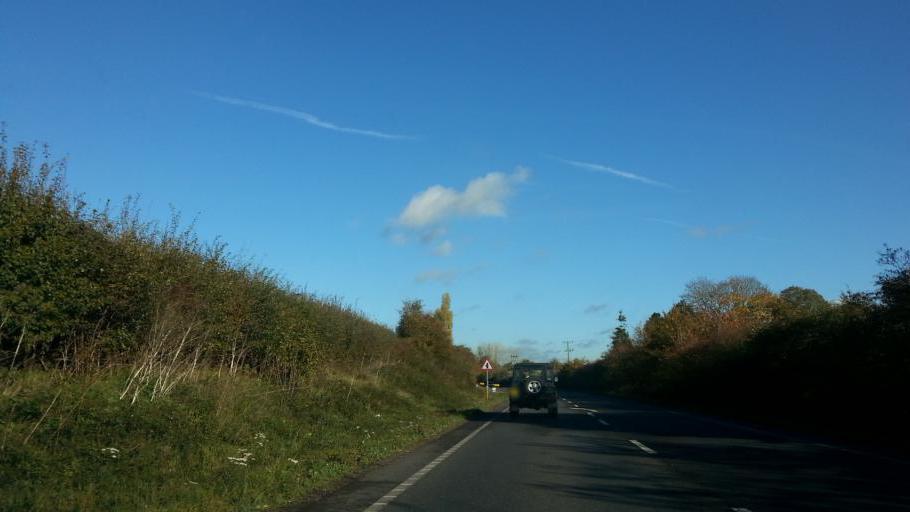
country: GB
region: England
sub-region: Norfolk
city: Harleston
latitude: 52.4152
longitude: 1.3416
